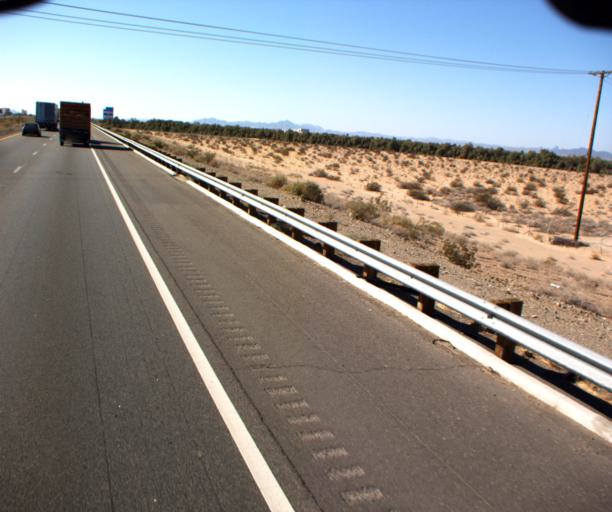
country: US
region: Arizona
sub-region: Yuma County
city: Fortuna Foothills
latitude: 32.6752
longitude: -114.4951
